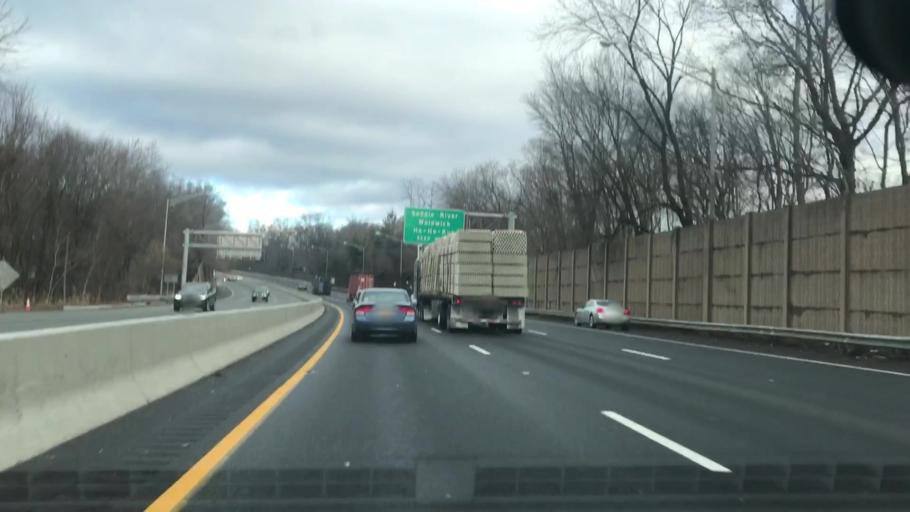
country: US
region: New Jersey
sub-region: Bergen County
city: Ho-Ho-Kus
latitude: 41.0040
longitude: -74.1019
